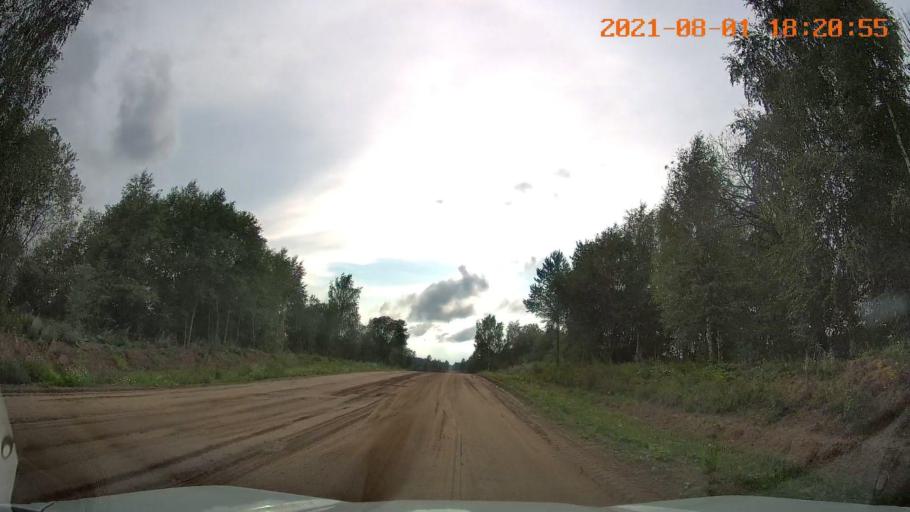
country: RU
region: Leningrad
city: Voznesen'ye
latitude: 60.8656
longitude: 35.5203
